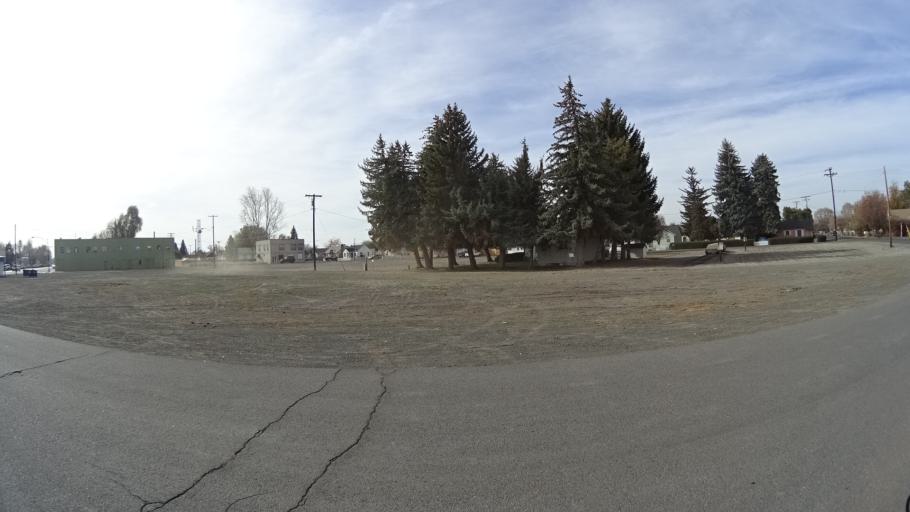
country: US
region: California
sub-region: Siskiyou County
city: Tulelake
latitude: 41.9582
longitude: -121.4770
